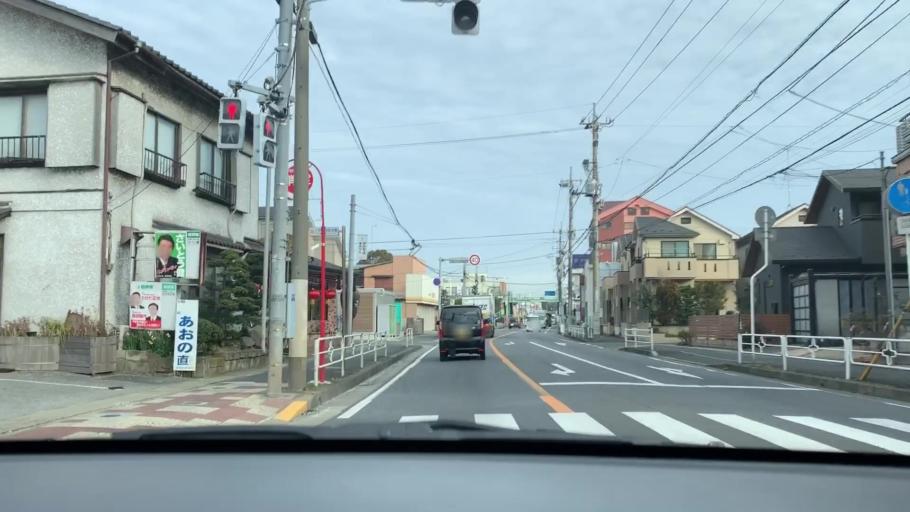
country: JP
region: Chiba
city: Nagareyama
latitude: 35.8518
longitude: 139.8989
